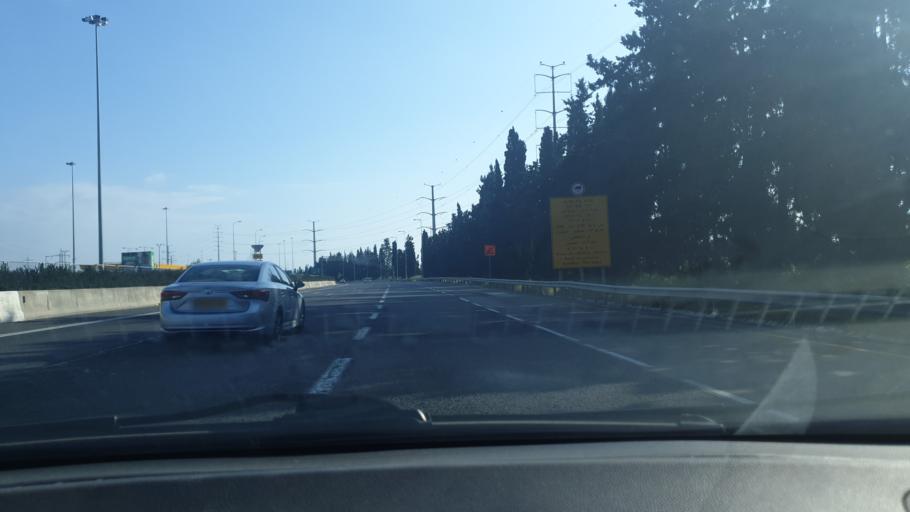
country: IL
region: Central District
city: Bet Dagan
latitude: 32.0013
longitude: 34.8069
